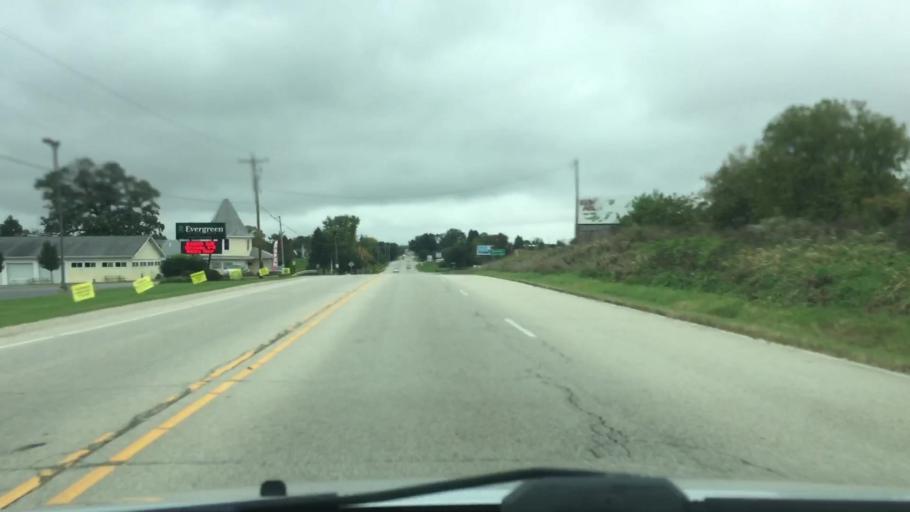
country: US
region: Wisconsin
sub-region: Walworth County
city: Elkhorn
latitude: 42.7198
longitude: -88.5425
